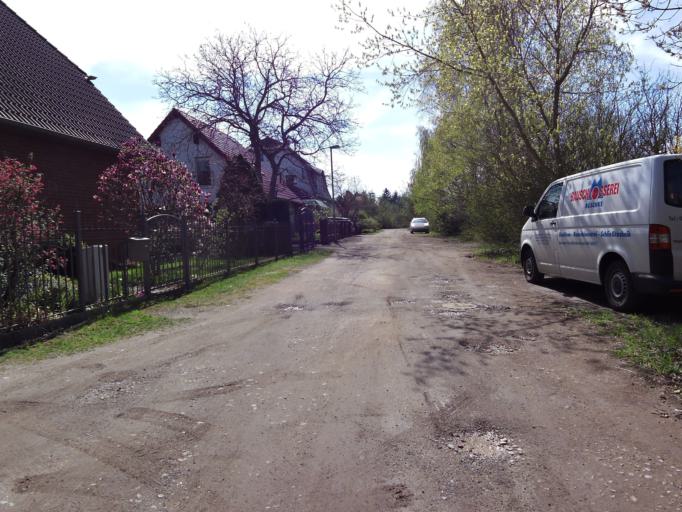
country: DE
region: Saxony
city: Markranstadt
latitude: 51.3166
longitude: 12.2694
